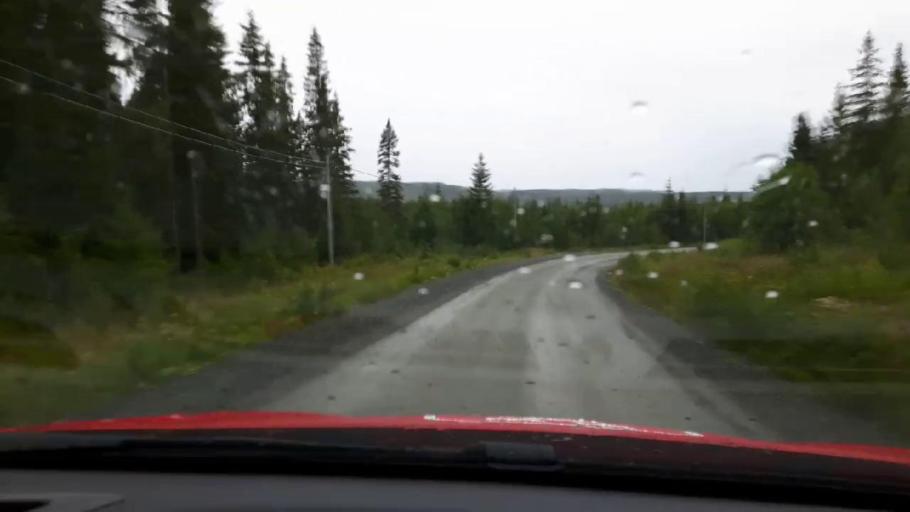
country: SE
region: Jaemtland
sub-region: Are Kommun
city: Are
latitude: 63.4799
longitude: 12.7993
